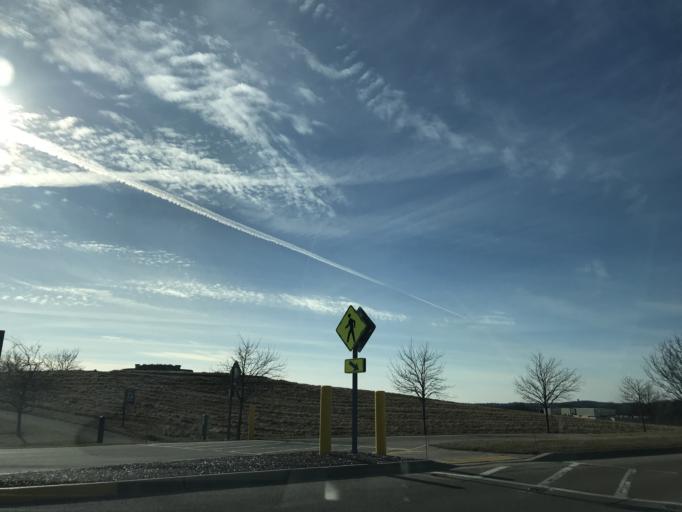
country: US
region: Wisconsin
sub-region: Dane County
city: Windsor
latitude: 43.1539
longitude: -89.2937
